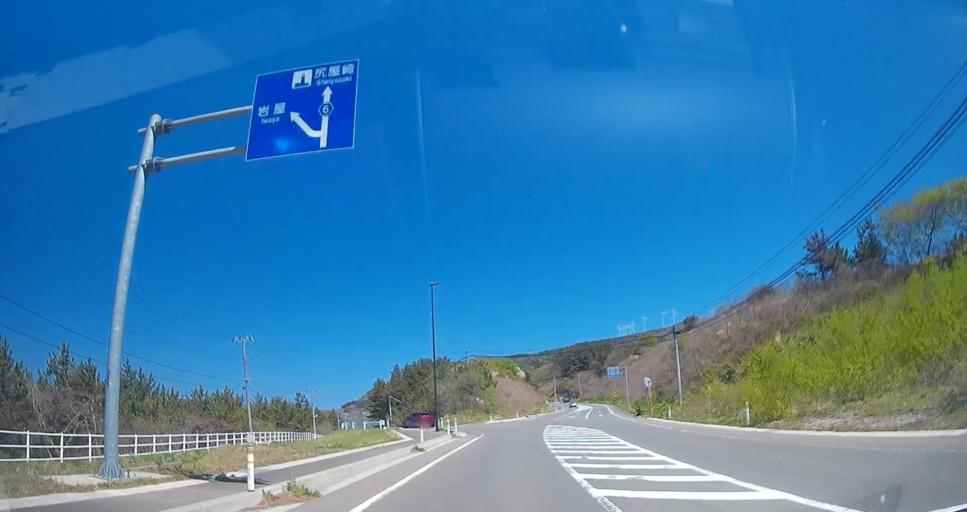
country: JP
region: Aomori
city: Mutsu
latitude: 41.3803
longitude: 141.3996
